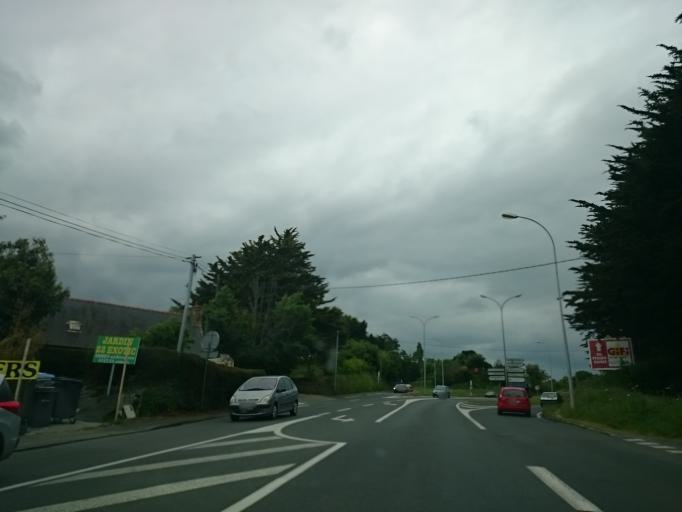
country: FR
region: Brittany
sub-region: Departement des Cotes-d'Armor
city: Lannion
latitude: 48.7375
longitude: -3.4678
